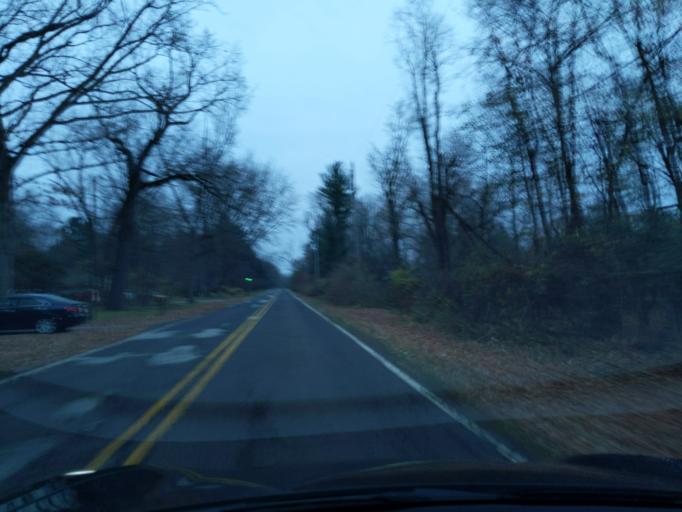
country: US
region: Indiana
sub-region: Saint Joseph County
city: Georgetown
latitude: 41.7284
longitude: -86.2555
